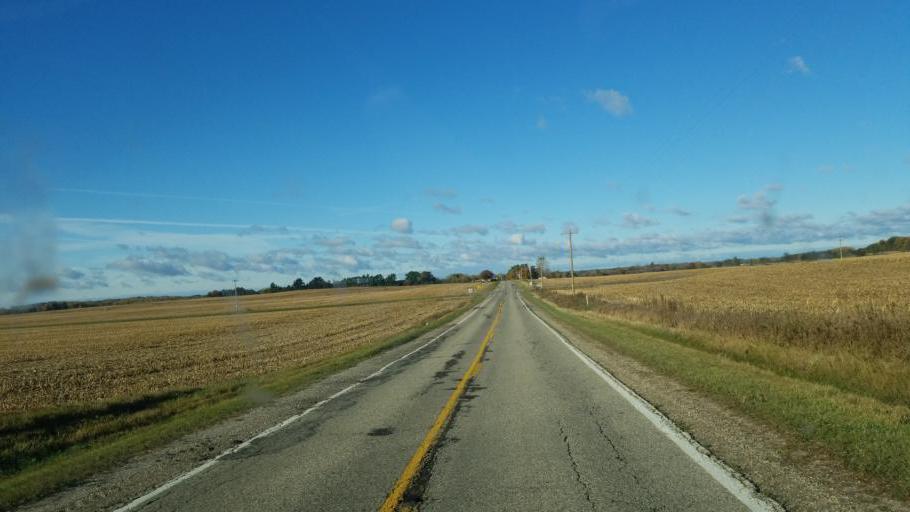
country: US
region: Michigan
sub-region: Montcalm County
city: Edmore
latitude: 43.4663
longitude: -85.1021
